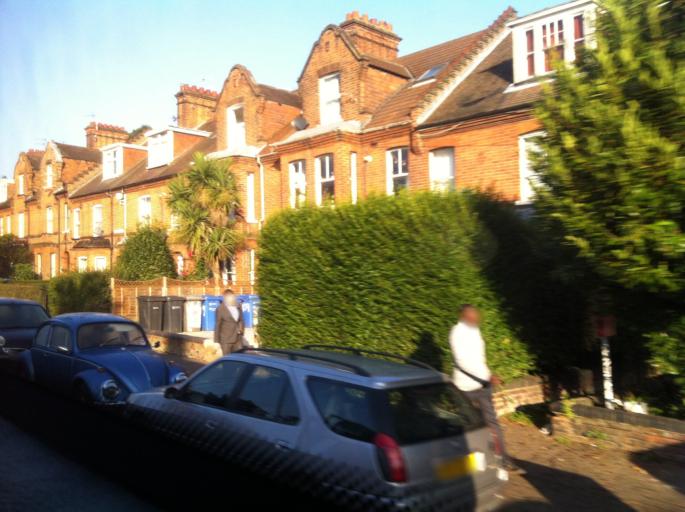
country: GB
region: England
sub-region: Norfolk
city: Norwich
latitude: 52.6304
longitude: 1.2749
